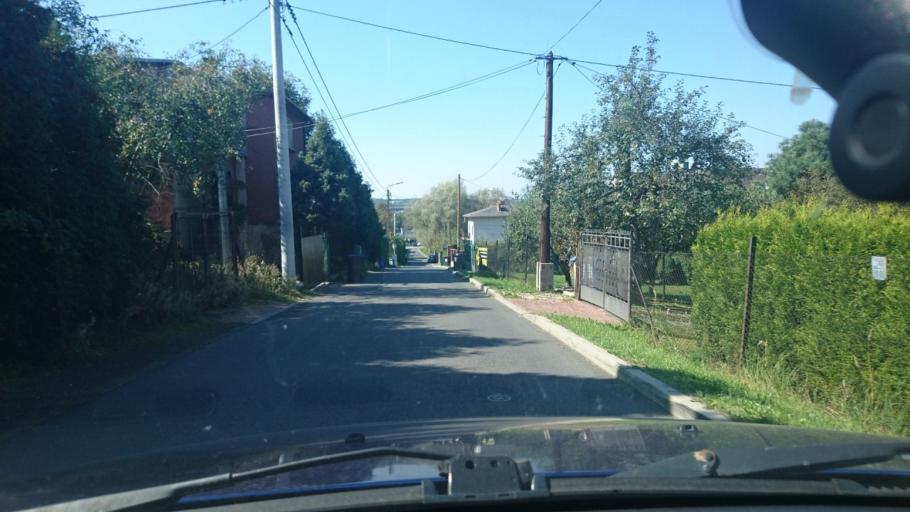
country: PL
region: Silesian Voivodeship
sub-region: Bielsko-Biala
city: Bielsko-Biala
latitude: 49.8428
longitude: 19.0588
